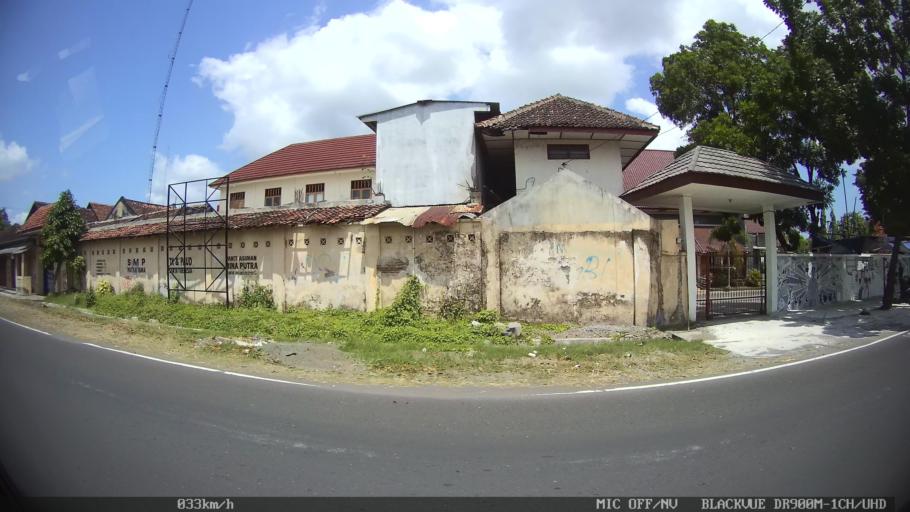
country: ID
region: Daerah Istimewa Yogyakarta
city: Bantul
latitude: -7.8800
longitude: 110.3367
